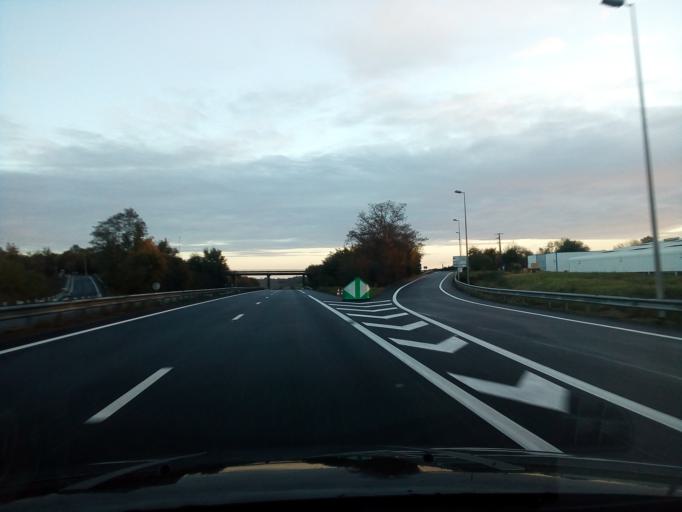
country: FR
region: Poitou-Charentes
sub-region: Departement de la Charente-Maritime
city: Montlieu-la-Garde
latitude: 45.2411
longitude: -0.2727
